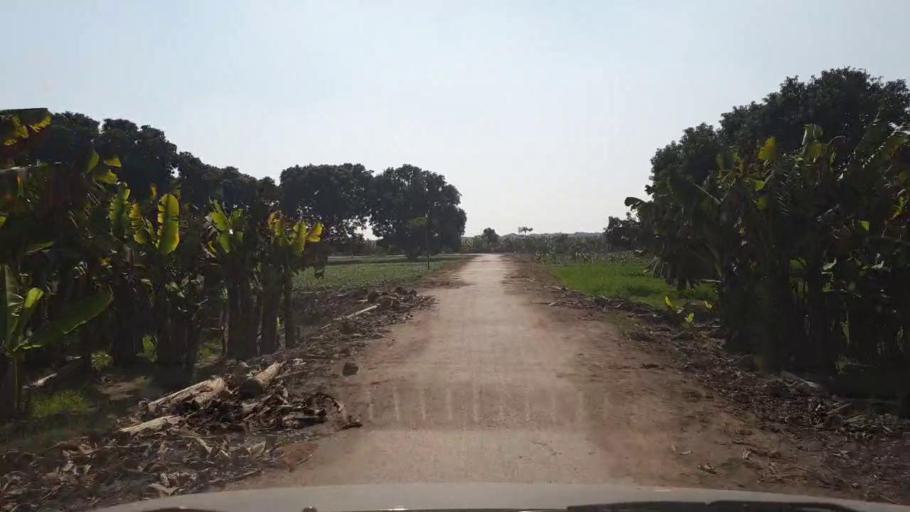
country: PK
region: Sindh
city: Tando Allahyar
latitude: 25.4143
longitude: 68.6342
